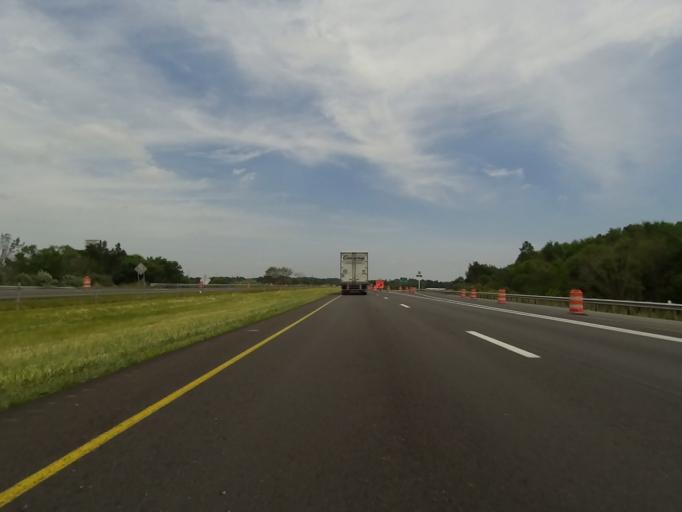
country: US
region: Ohio
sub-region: Portage County
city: Ravenna
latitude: 41.1057
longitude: -81.1611
